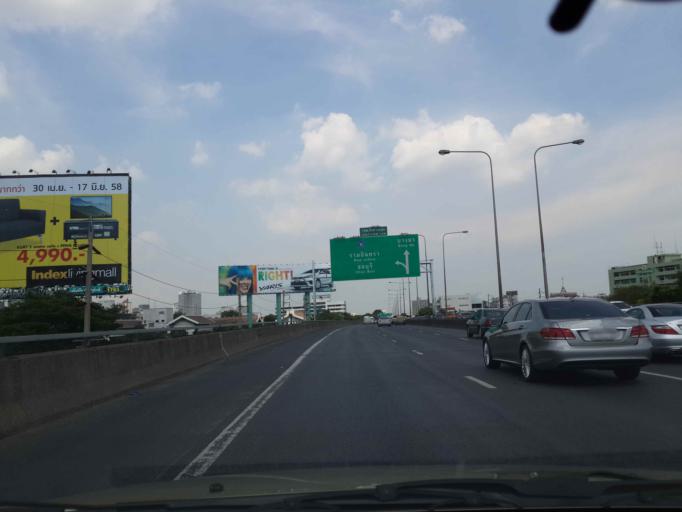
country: TH
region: Bangkok
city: Khlong Toei
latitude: 13.7102
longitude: 100.5818
